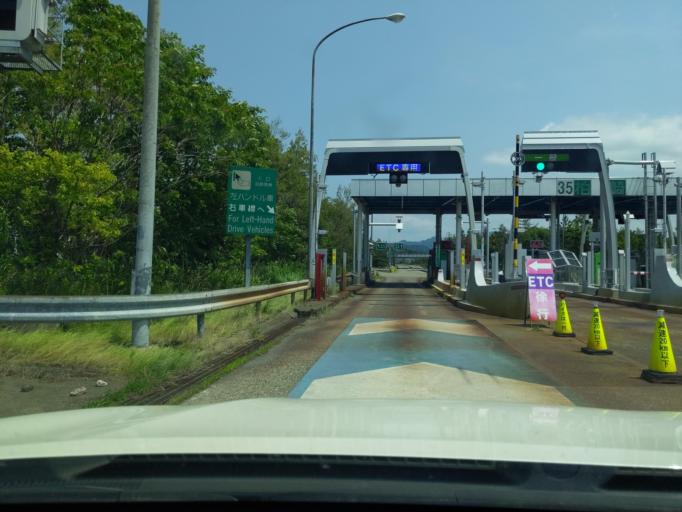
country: JP
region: Niigata
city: Kashiwazaki
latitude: 37.3618
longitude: 138.5902
